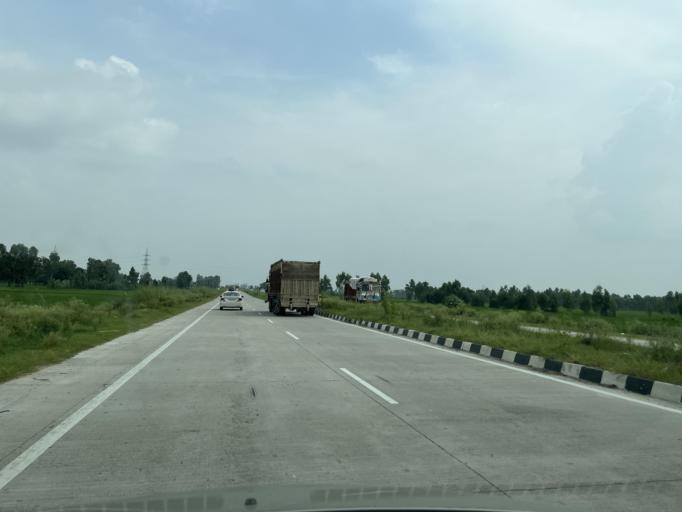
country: IN
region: Uttarakhand
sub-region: Udham Singh Nagar
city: Kashipur
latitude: 29.1703
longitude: 78.9526
